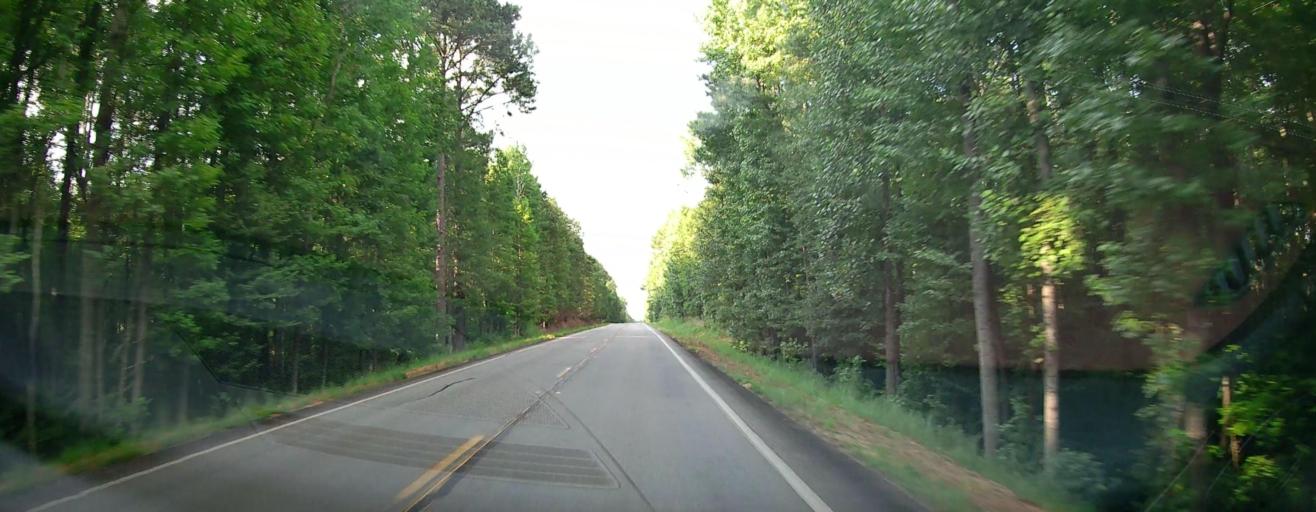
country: US
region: Georgia
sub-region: Crawford County
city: Knoxville
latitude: 32.8251
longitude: -84.0202
